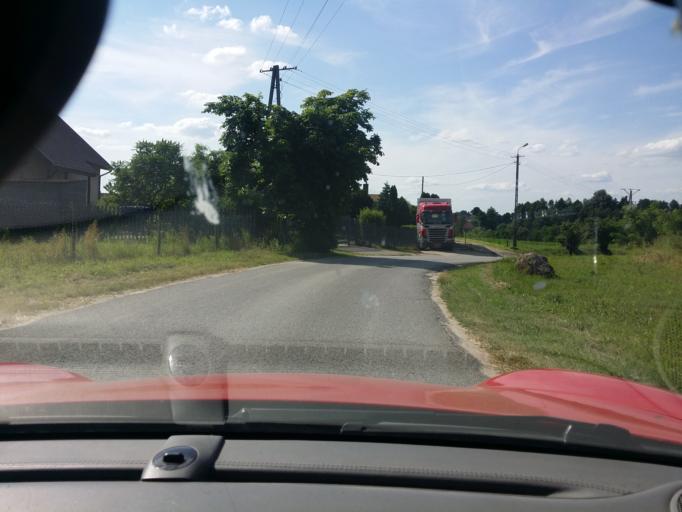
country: PL
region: Masovian Voivodeship
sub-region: Powiat radomski
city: Trablice
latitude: 51.3480
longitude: 21.1372
